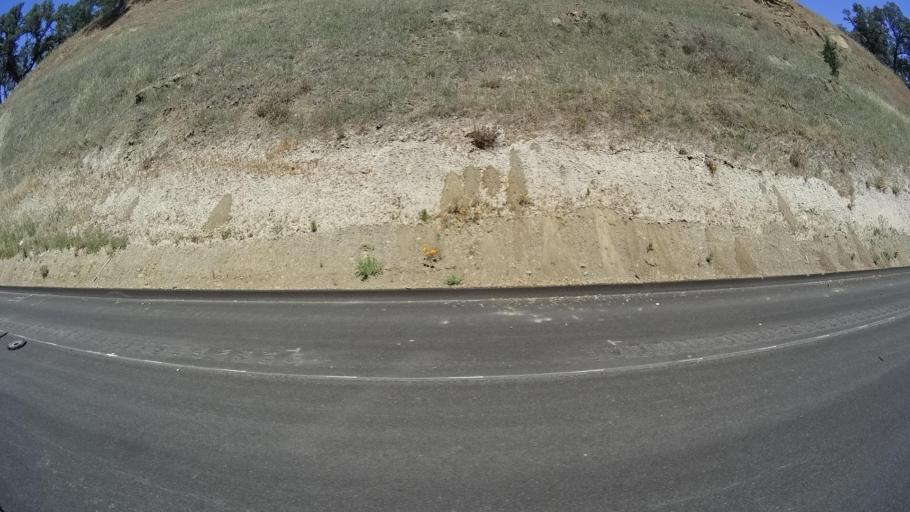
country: US
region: California
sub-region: Lake County
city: Hidden Valley Lake
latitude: 38.8408
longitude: -122.6025
